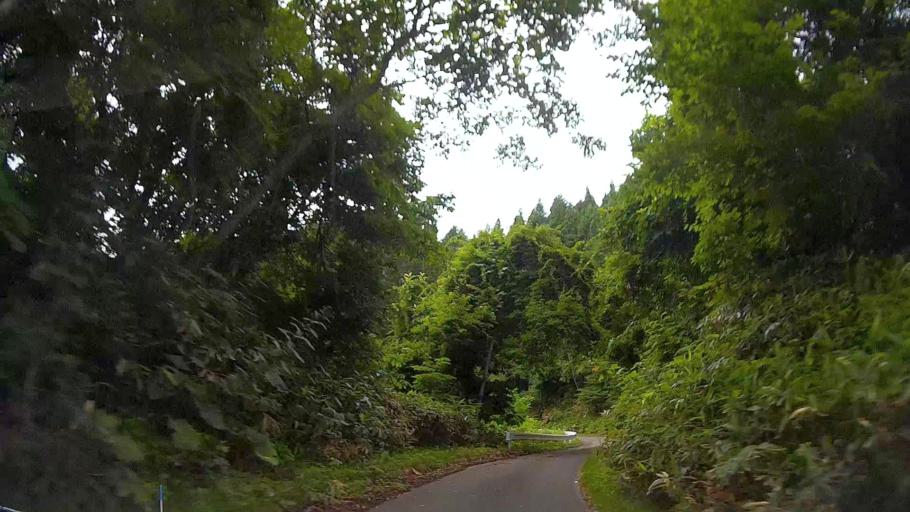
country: JP
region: Hokkaido
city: Nanae
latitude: 42.1252
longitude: 140.4219
